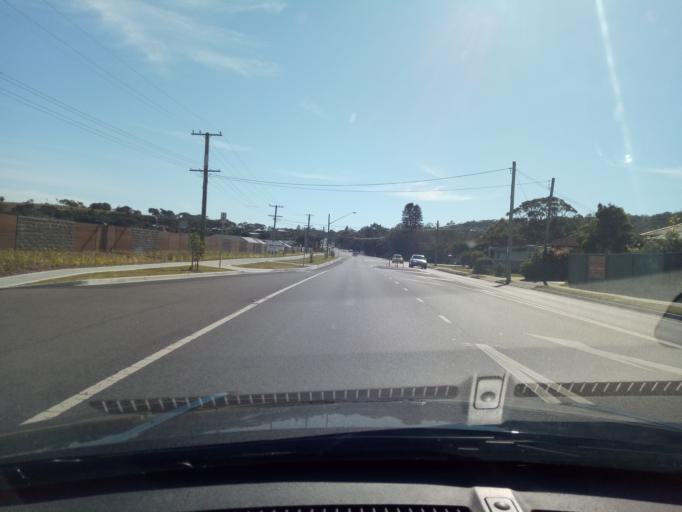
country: AU
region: New South Wales
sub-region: Gosford Shire
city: Forresters Beach
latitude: -33.4057
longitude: 151.4651
